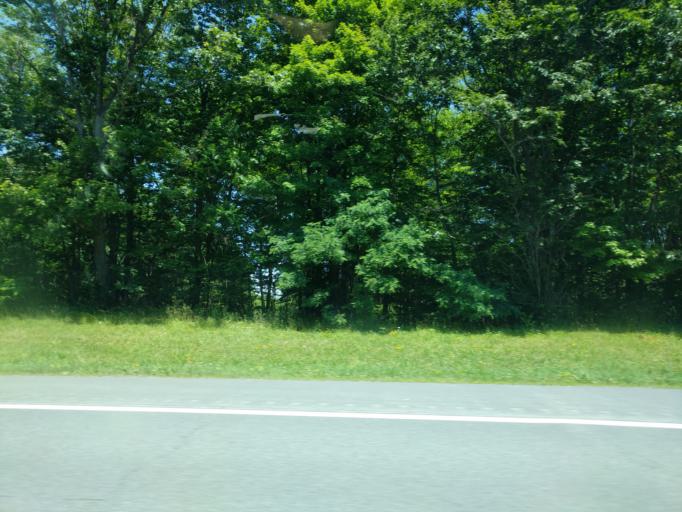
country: US
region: New York
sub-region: Sullivan County
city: Monticello
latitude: 41.6621
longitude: -74.6760
